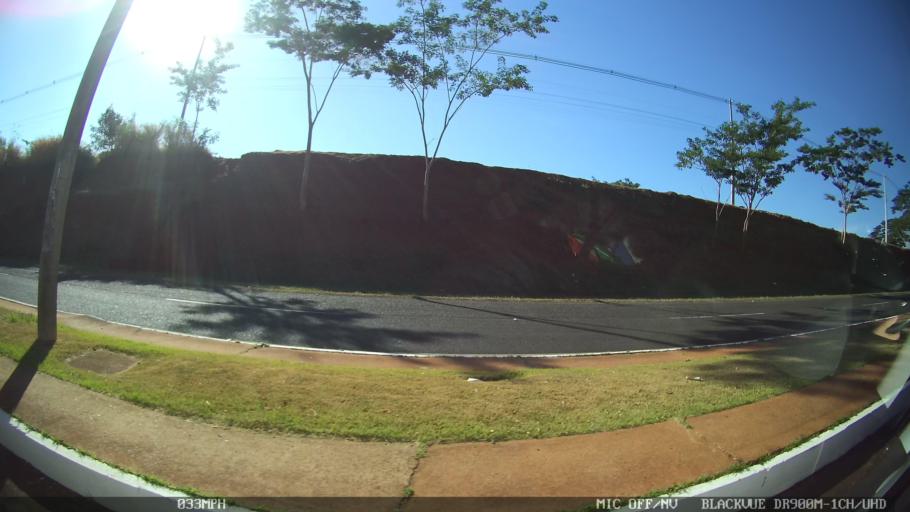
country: BR
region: Sao Paulo
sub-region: Olimpia
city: Olimpia
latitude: -20.7385
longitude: -48.8980
